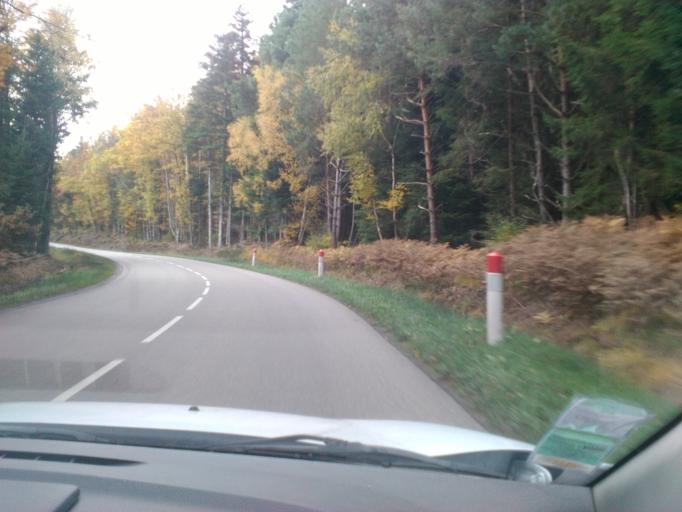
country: FR
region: Lorraine
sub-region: Departement des Vosges
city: Etival-Clairefontaine
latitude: 48.3843
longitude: 6.8013
